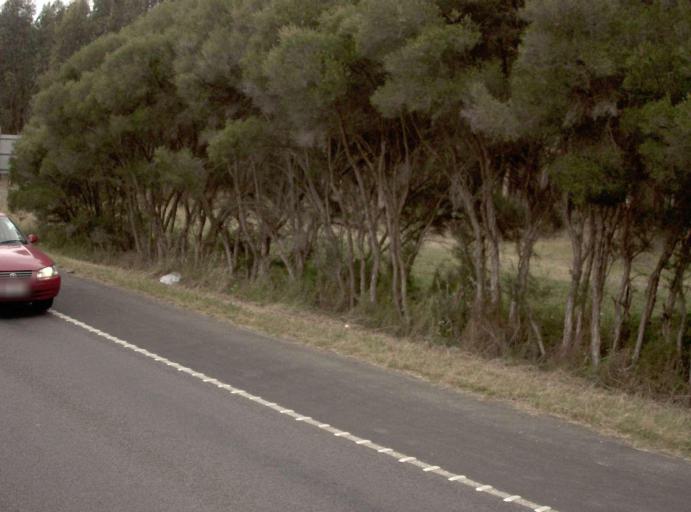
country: AU
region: Victoria
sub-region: Latrobe
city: Morwell
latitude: -38.2905
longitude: 146.4149
